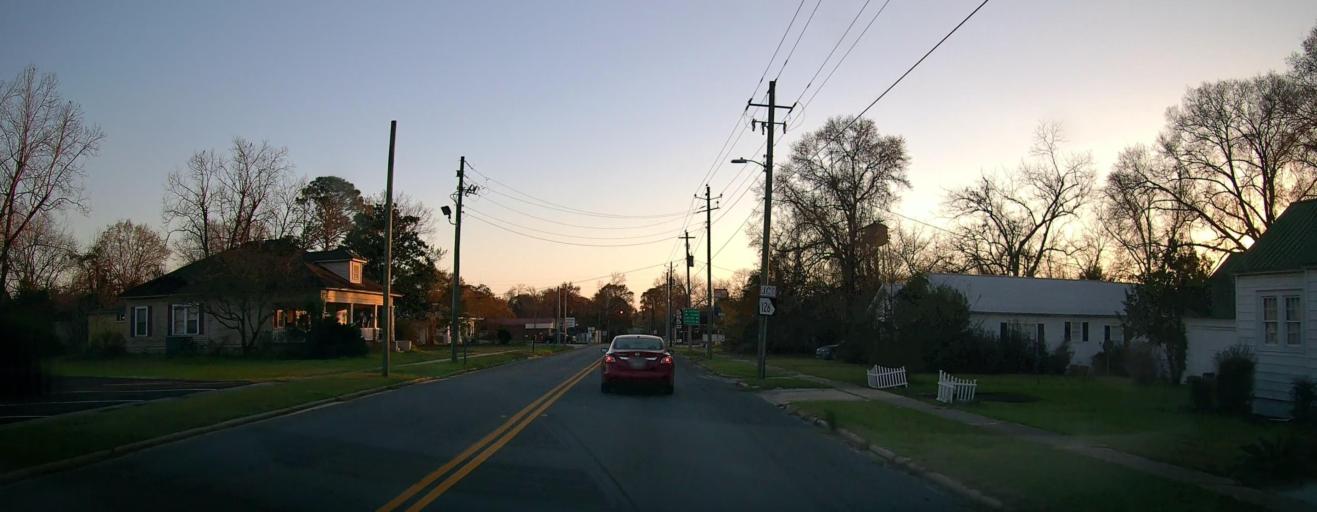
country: US
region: Georgia
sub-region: Dodge County
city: Chester
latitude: 32.3406
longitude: -83.0415
